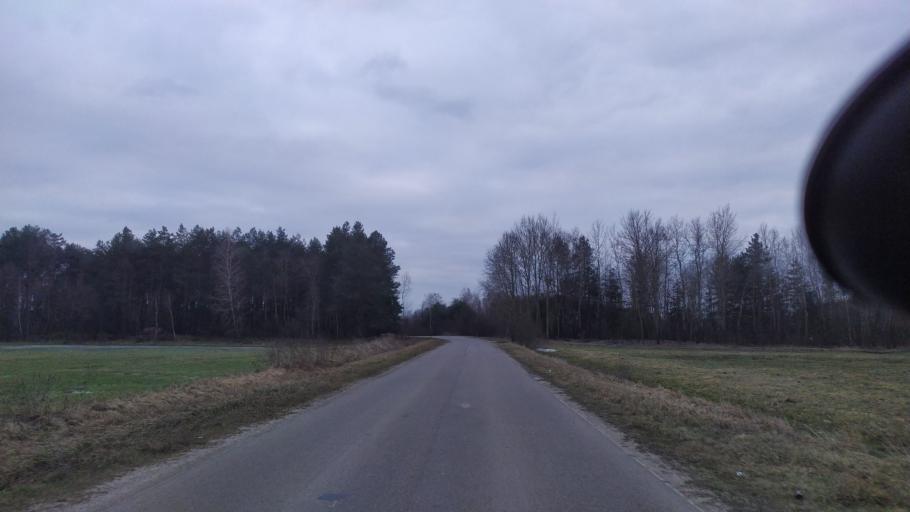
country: PL
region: Lublin Voivodeship
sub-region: Powiat lubartowski
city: Abramow
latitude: 51.4274
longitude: 22.3146
